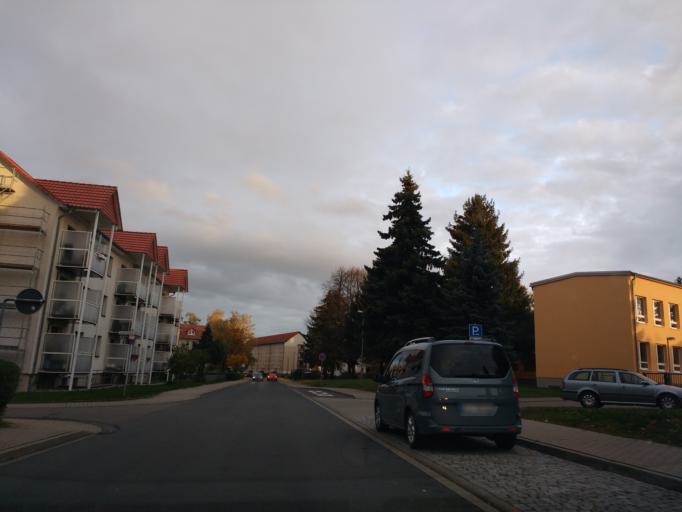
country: DE
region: Thuringia
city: Leinefelde
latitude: 51.3867
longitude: 10.3241
